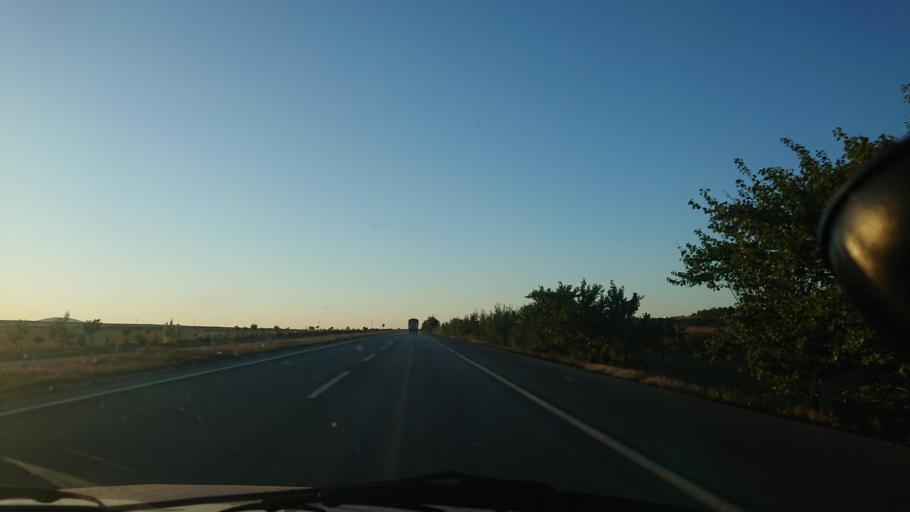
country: TR
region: Eskisehir
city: Mahmudiye
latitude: 39.4919
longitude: 30.9770
